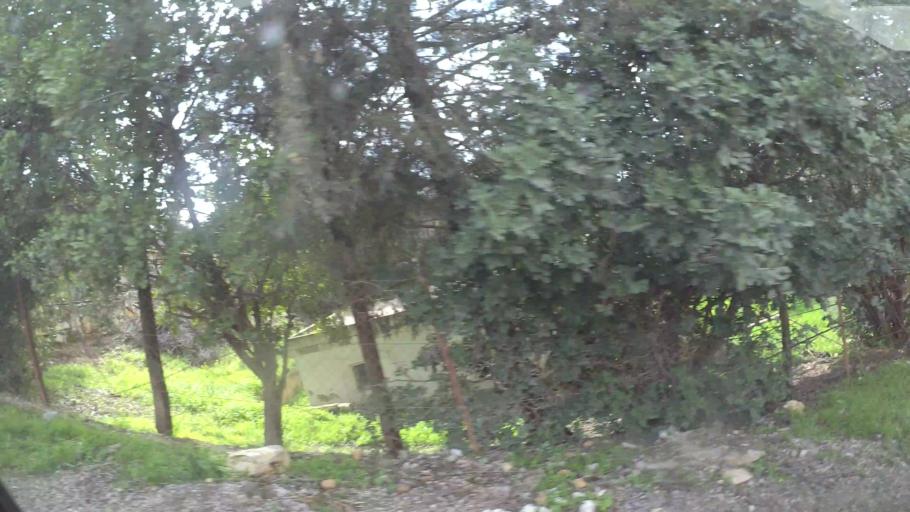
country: JO
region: Amman
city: Al Jubayhah
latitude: 32.0345
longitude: 35.8156
